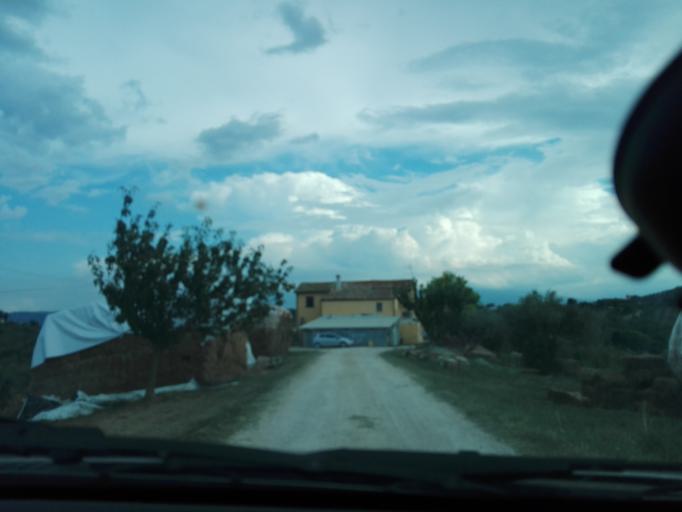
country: IT
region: Abruzzo
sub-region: Provincia di Pescara
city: Cappelle sul Tavo
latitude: 42.4490
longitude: 14.1008
